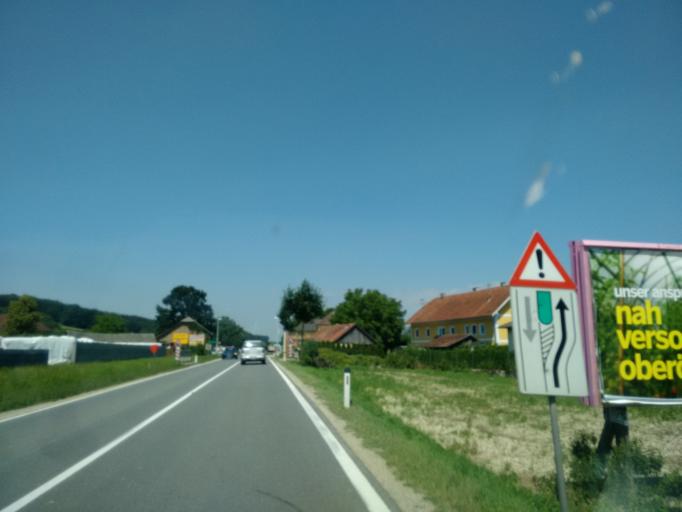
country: AT
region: Upper Austria
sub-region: Wels-Land
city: Buchkirchen
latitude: 48.2615
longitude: 13.9777
